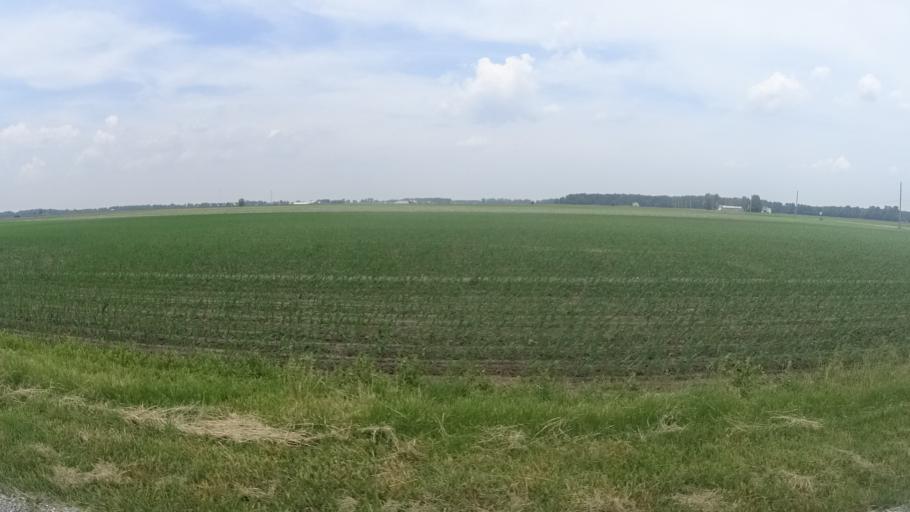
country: US
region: Ohio
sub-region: Huron County
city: Monroeville
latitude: 41.2908
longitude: -82.6723
